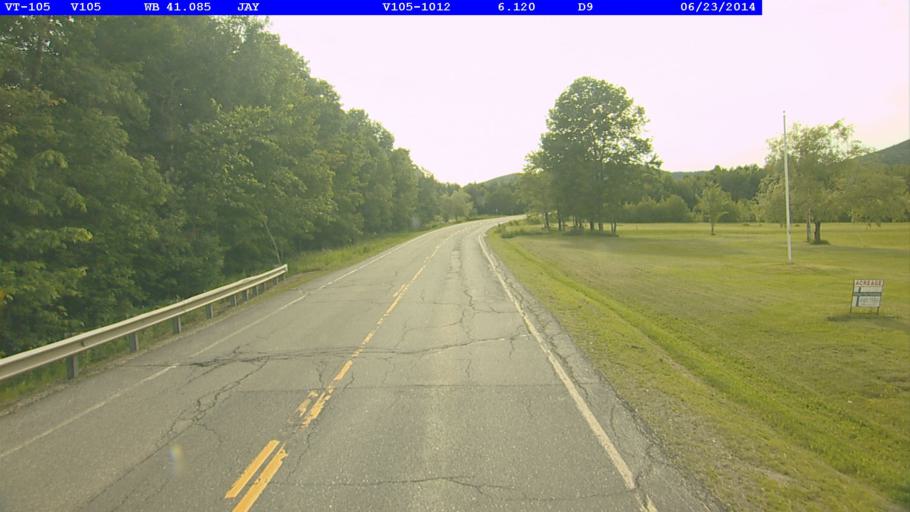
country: CA
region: Quebec
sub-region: Monteregie
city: Sutton
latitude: 44.9729
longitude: -72.4653
